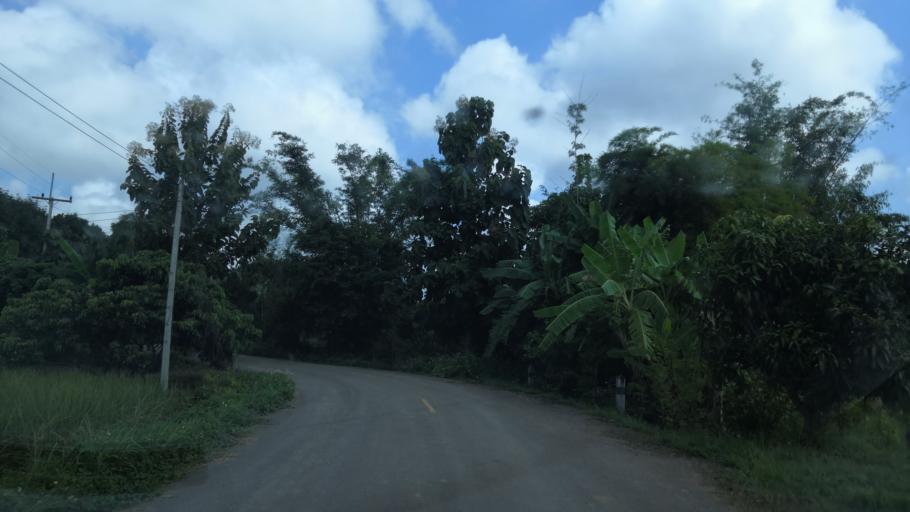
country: TH
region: Chiang Rai
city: Wiang Chiang Rung
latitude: 20.0224
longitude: 100.0446
